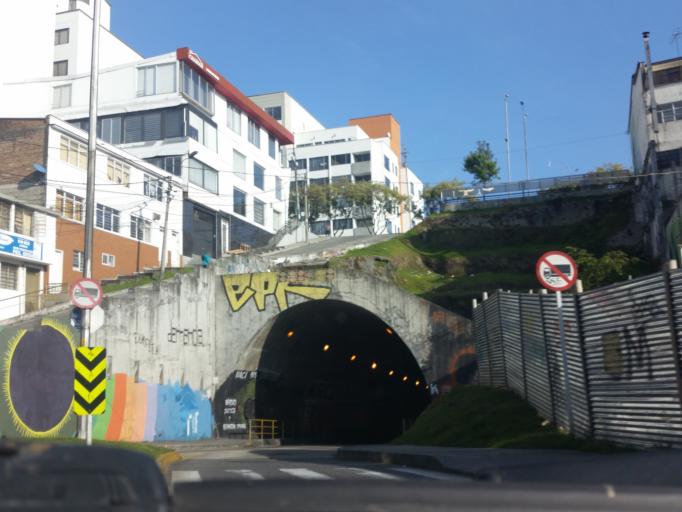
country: CO
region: Caldas
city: Manizales
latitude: 5.0634
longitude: -75.4967
